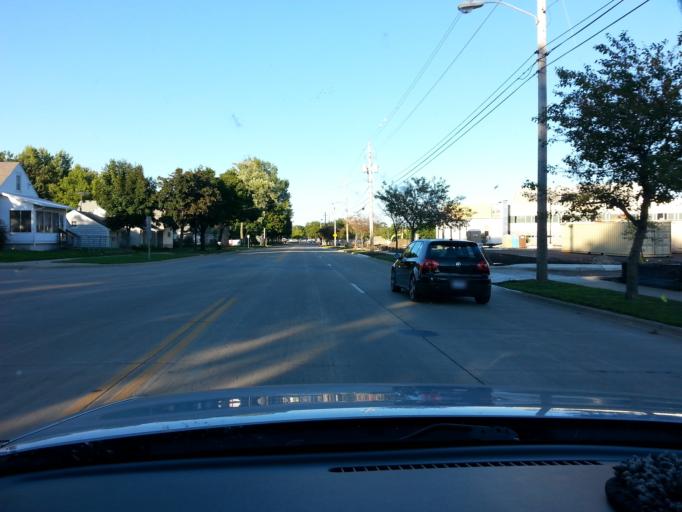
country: US
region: Minnesota
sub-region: Olmsted County
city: Rochester
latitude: 44.0199
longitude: -92.4423
